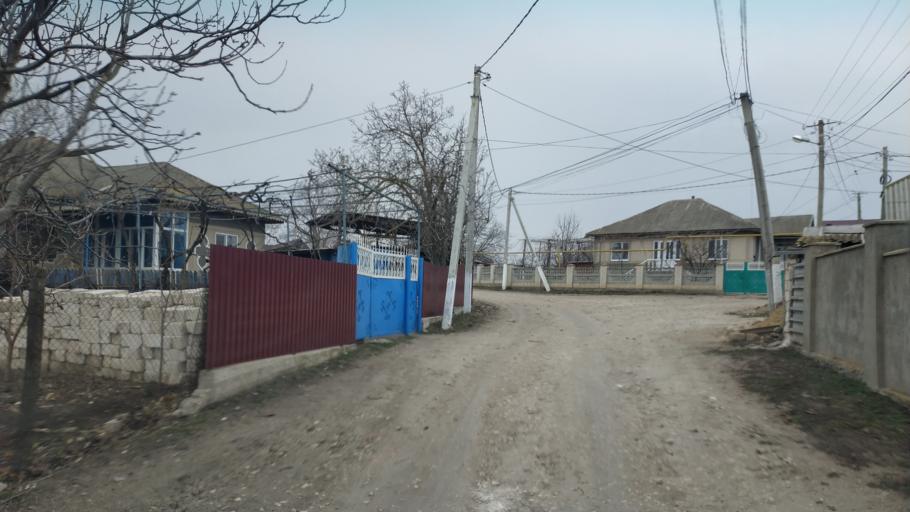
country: MD
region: Chisinau
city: Singera
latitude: 46.8256
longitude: 29.0230
